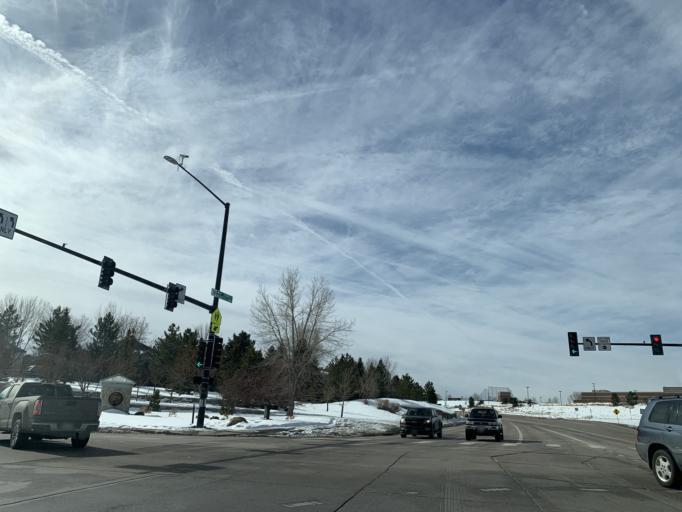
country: US
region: Colorado
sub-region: Douglas County
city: Carriage Club
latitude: 39.5213
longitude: -104.9174
